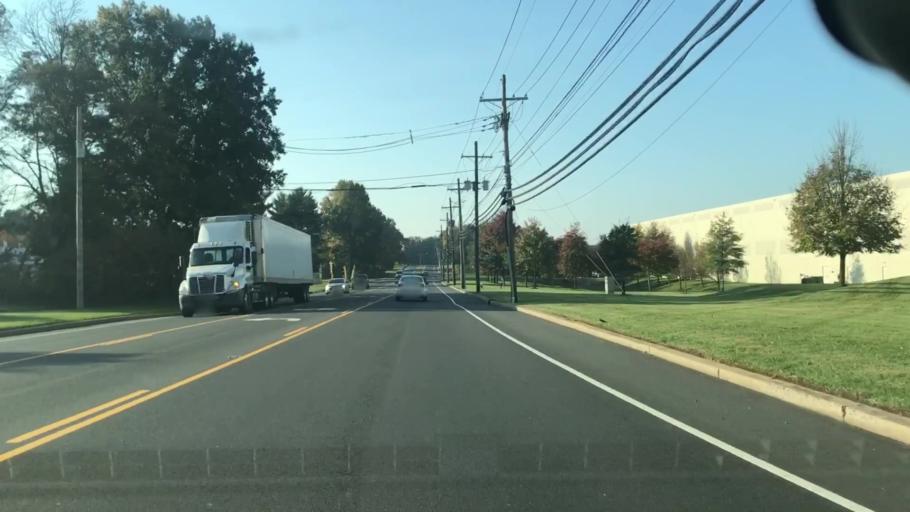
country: US
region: New Jersey
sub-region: Middlesex County
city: Rossmoor
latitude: 40.3431
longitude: -74.4833
